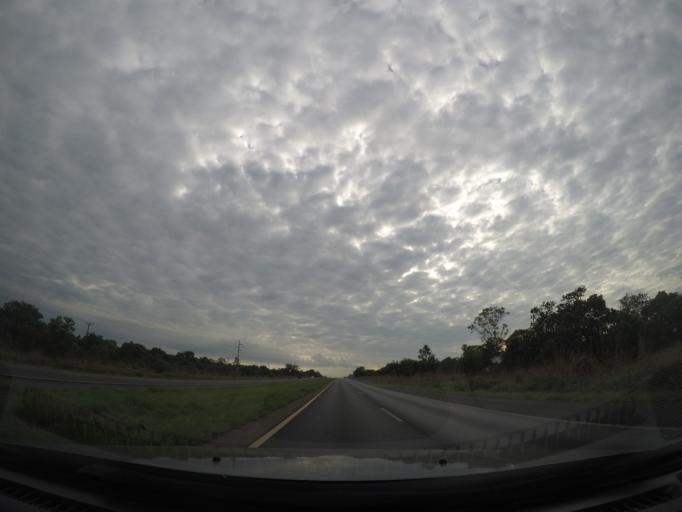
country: BR
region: Goias
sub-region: Planaltina
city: Planaltina
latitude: -15.5962
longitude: -47.6425
